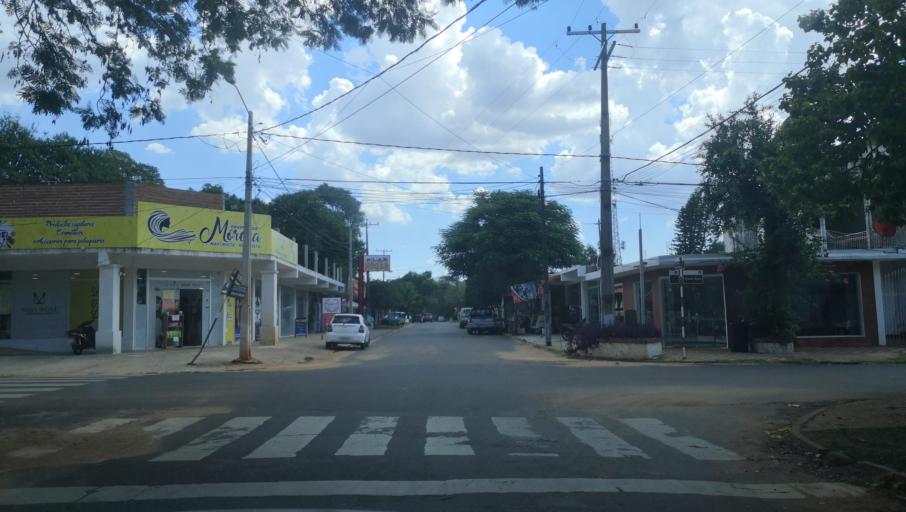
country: PY
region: Misiones
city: Santa Maria
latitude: -26.8886
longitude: -57.0243
